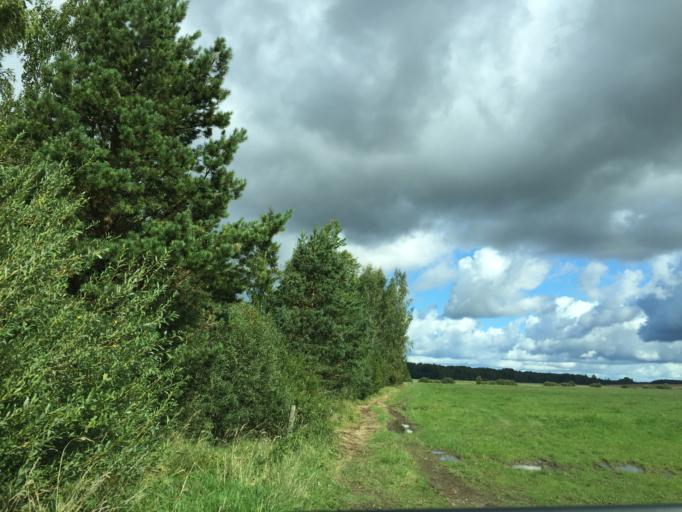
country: LV
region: Kuldigas Rajons
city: Kuldiga
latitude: 56.9952
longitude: 22.1183
